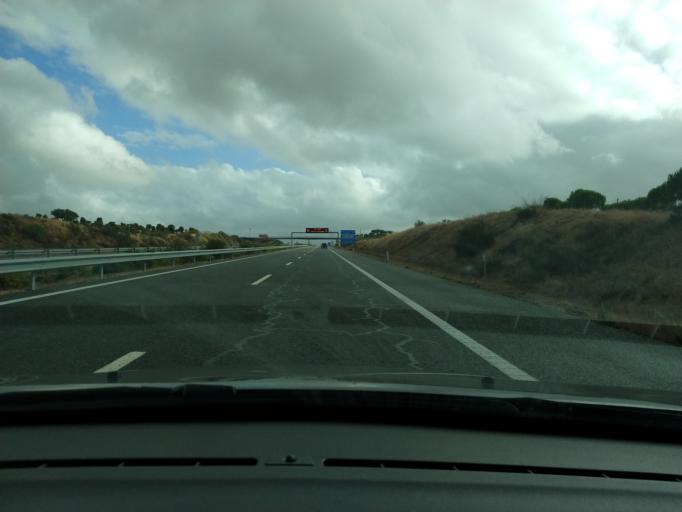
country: PT
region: Beja
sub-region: Ourique
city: Ourique
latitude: 37.5426
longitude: -8.1869
